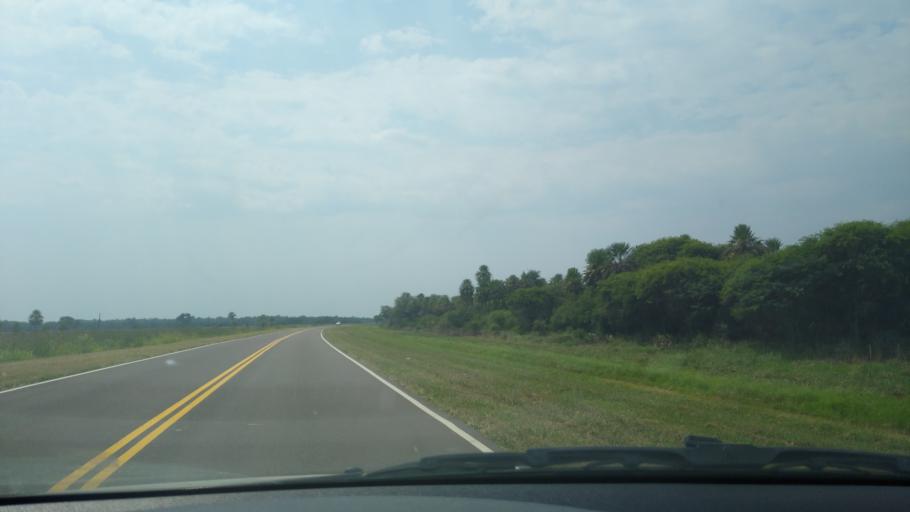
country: AR
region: Chaco
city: Margarita Belen
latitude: -27.0705
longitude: -58.9628
